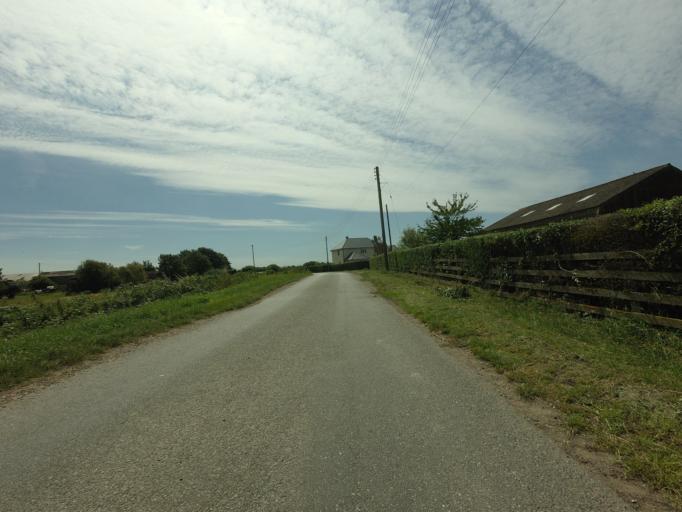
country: GB
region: England
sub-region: Kent
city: Stone
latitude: 51.0149
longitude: 0.7943
